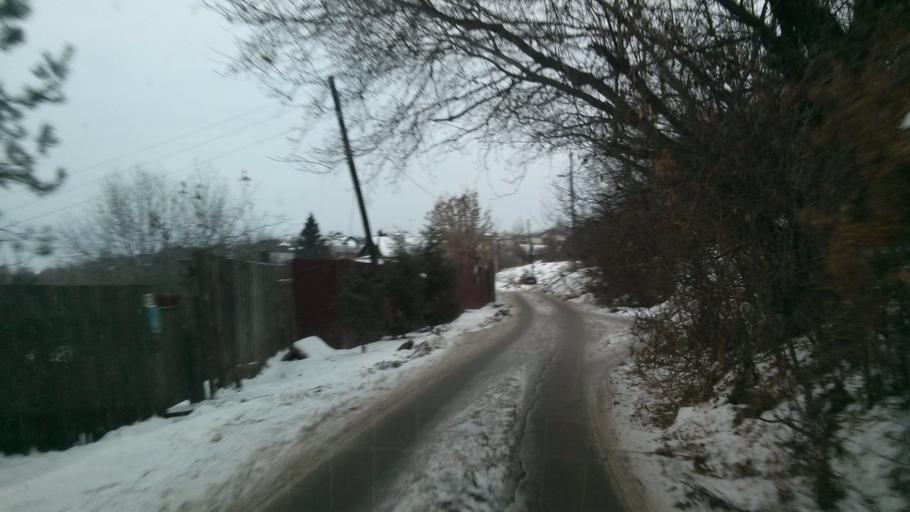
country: RU
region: Nizjnij Novgorod
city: Afonino
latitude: 56.2965
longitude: 44.0991
